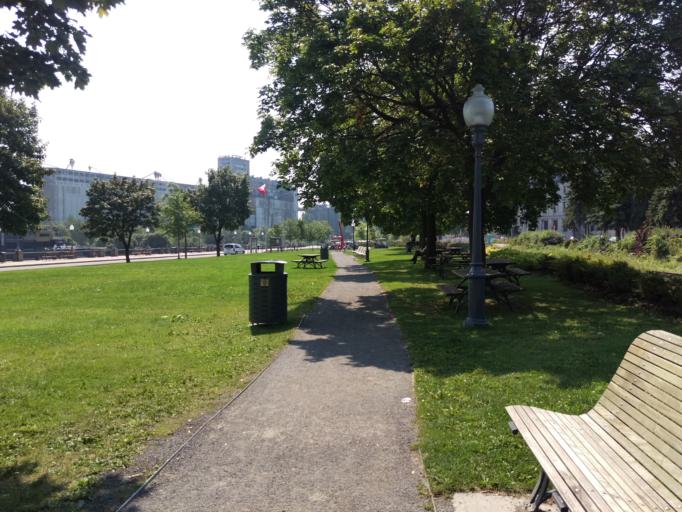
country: CA
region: Quebec
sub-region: Montreal
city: Montreal
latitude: 45.5013
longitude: -73.5533
